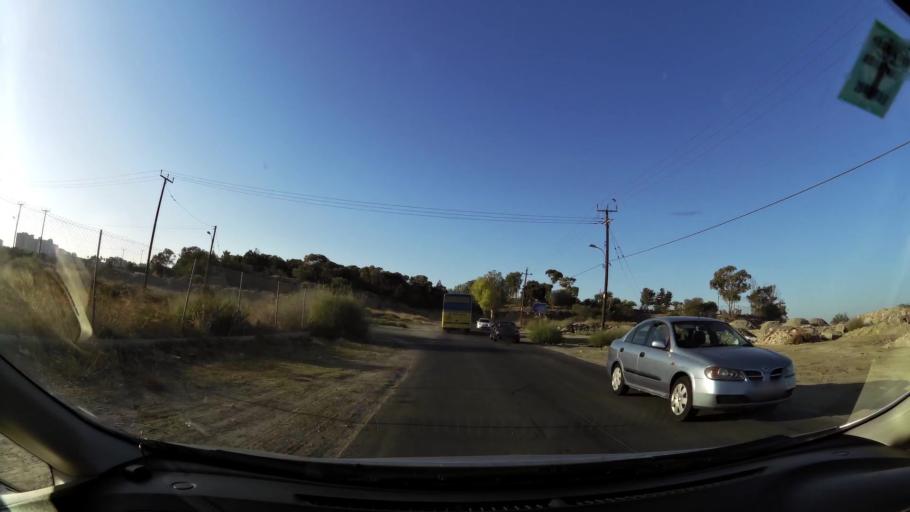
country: CY
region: Larnaka
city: Larnaca
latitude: 34.8981
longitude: 33.6330
